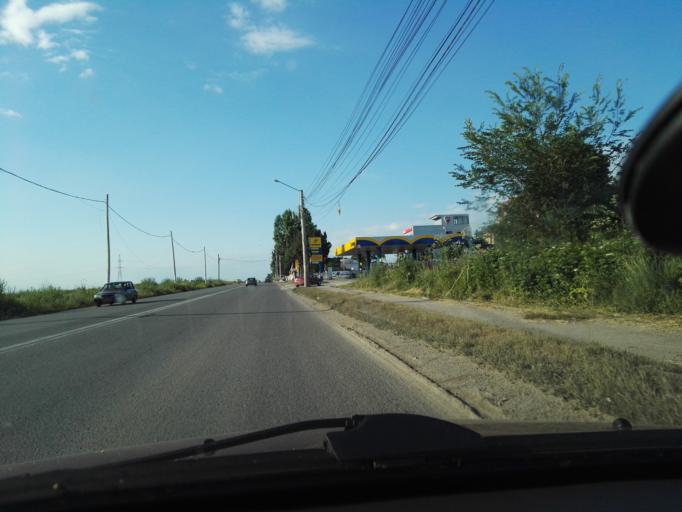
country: RO
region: Ilfov
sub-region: Comuna Jilava
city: Jilava
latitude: 44.3541
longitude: 26.0853
